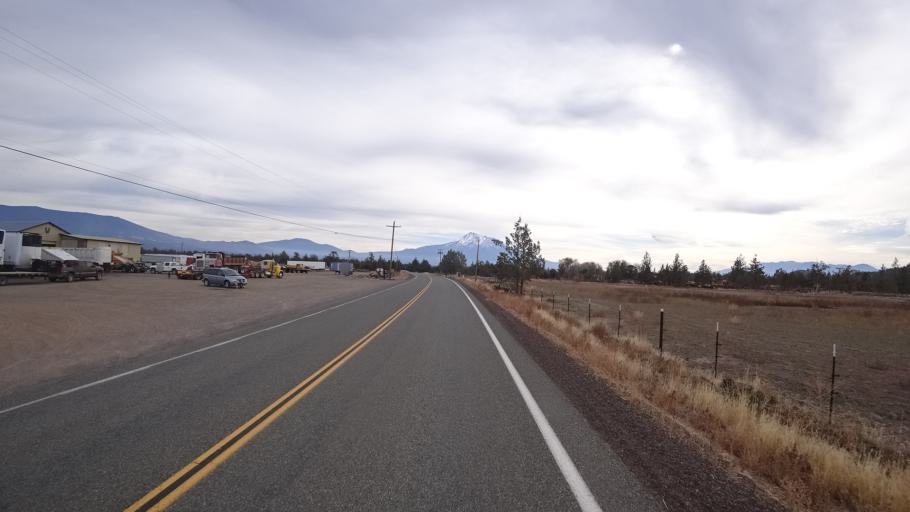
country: US
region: California
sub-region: Siskiyou County
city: Montague
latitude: 41.6288
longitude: -122.4322
